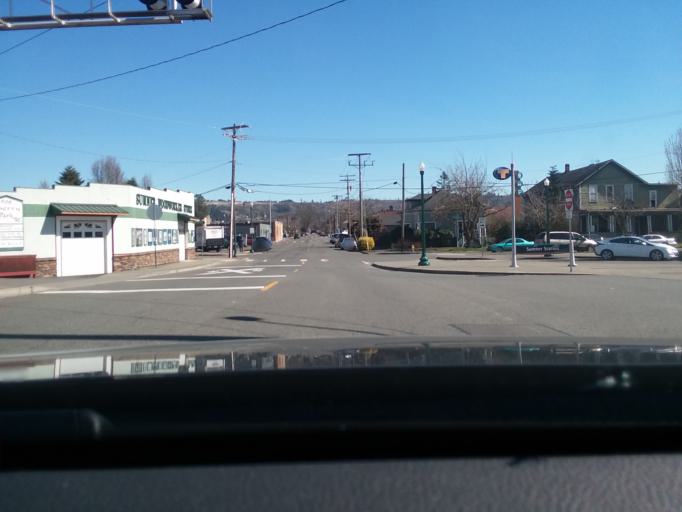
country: US
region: Washington
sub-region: Pierce County
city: Sumner
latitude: 47.2022
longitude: -122.2437
